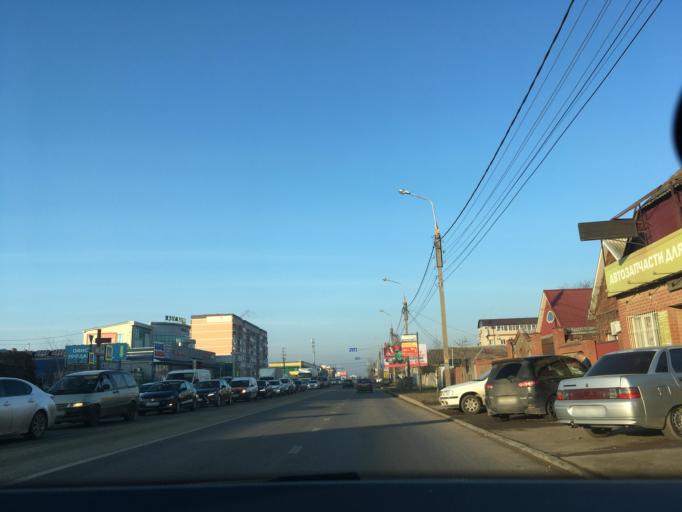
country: RU
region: Krasnodarskiy
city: Krasnodar
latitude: 45.1124
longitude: 39.0122
